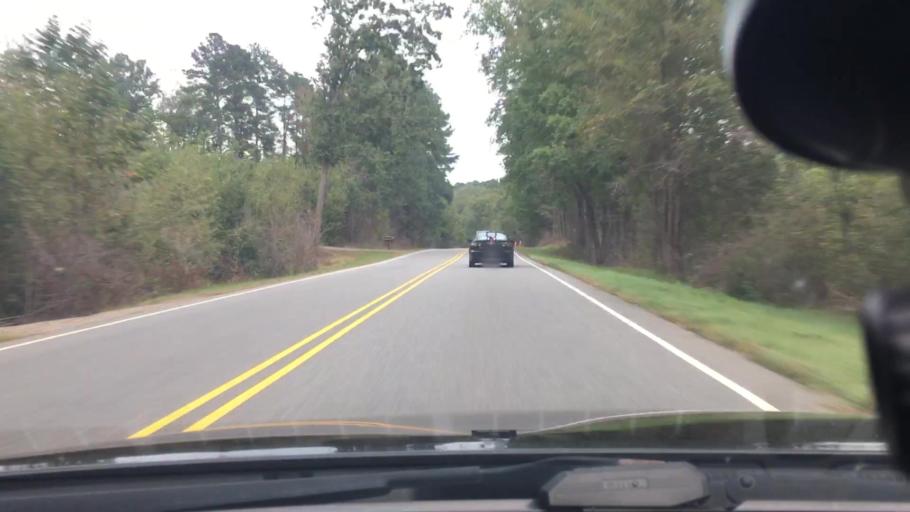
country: US
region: North Carolina
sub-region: Moore County
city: Robbins
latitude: 35.3898
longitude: -79.6447
